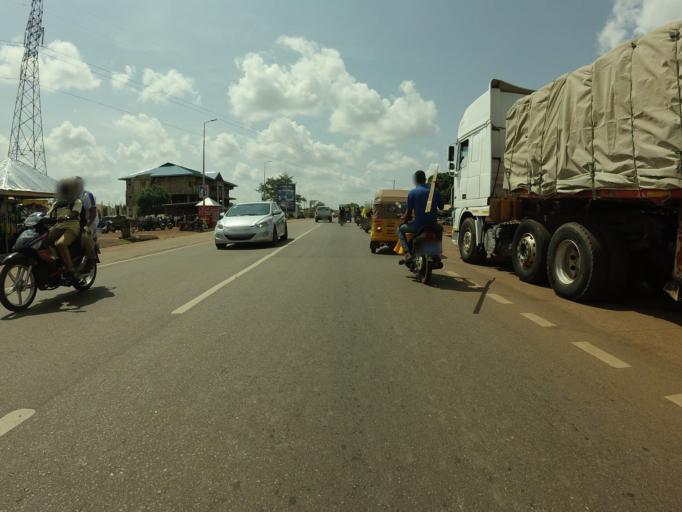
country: GH
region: Northern
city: Tamale
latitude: 9.4486
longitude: -0.8447
